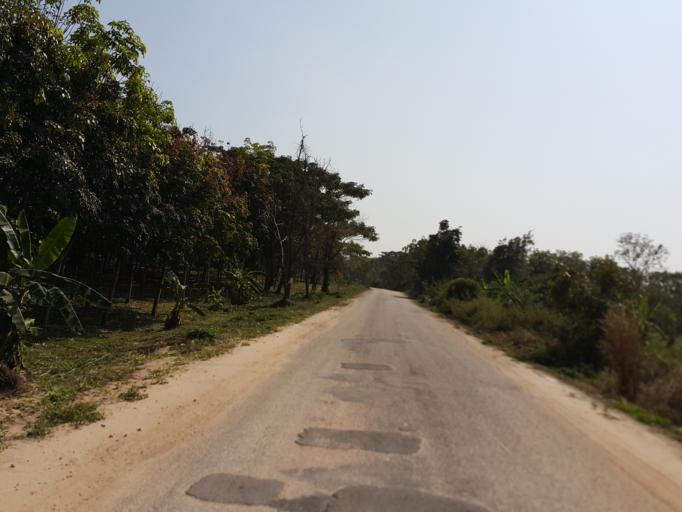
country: TH
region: Lampang
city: Wang Nuea
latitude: 19.0063
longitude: 99.6226
